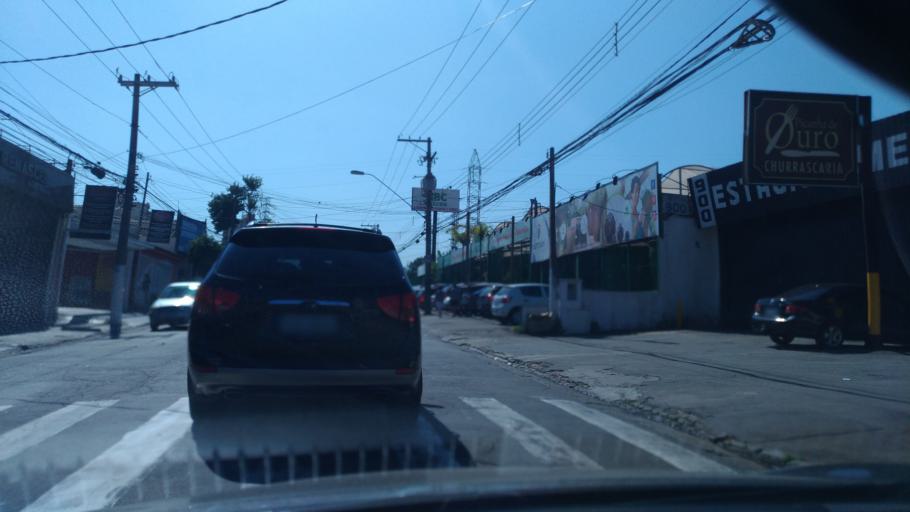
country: BR
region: Sao Paulo
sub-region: Santo Andre
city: Santo Andre
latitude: -23.6701
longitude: -46.5591
